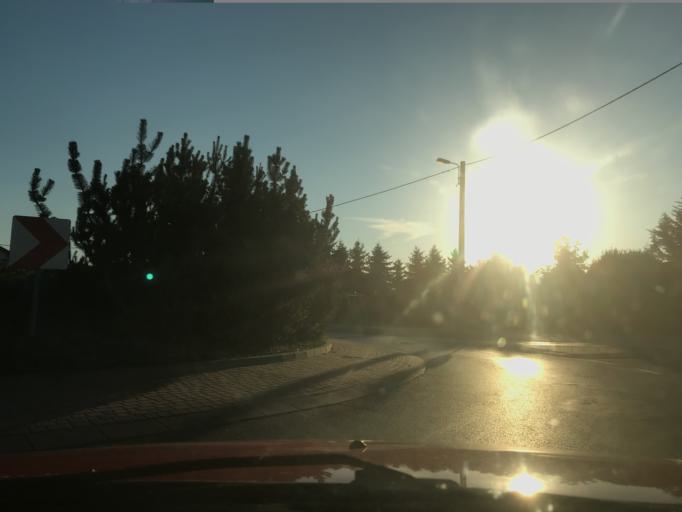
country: PL
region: Greater Poland Voivodeship
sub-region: Powiat poznanski
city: Tarnowo Podgorne
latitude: 52.4340
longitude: 16.7011
